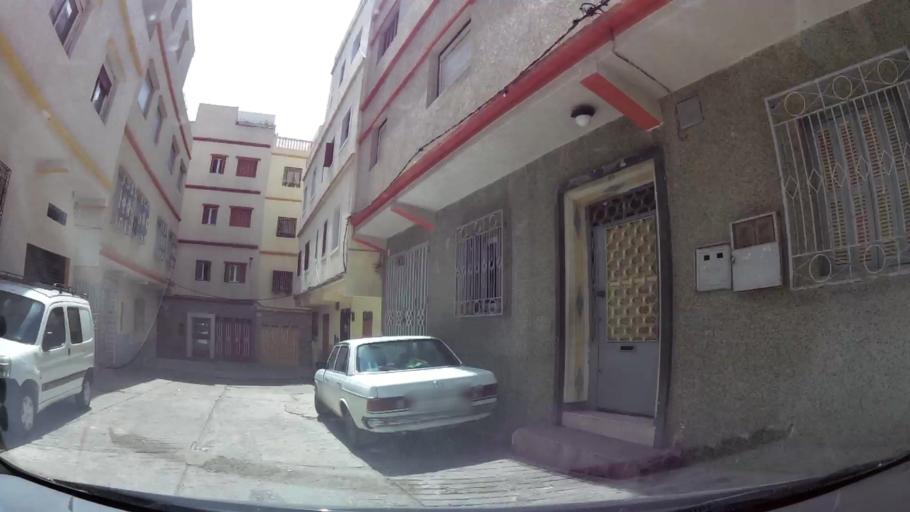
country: MA
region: Tanger-Tetouan
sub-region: Tanger-Assilah
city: Tangier
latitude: 35.7565
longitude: -5.8143
